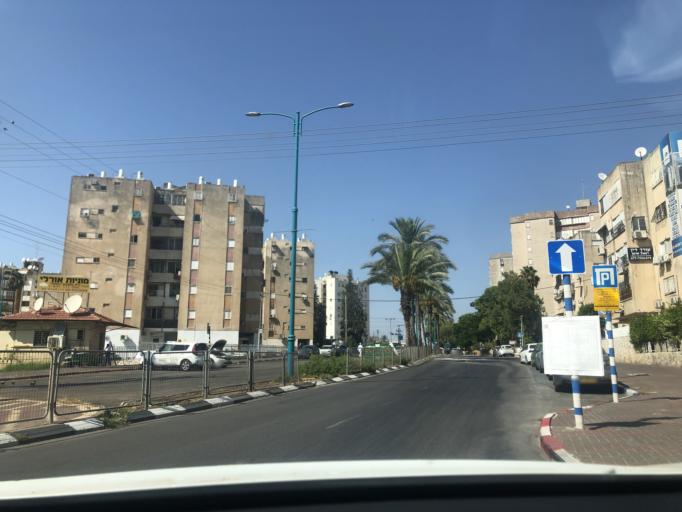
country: IL
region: Central District
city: Lod
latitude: 31.9467
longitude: 34.8926
